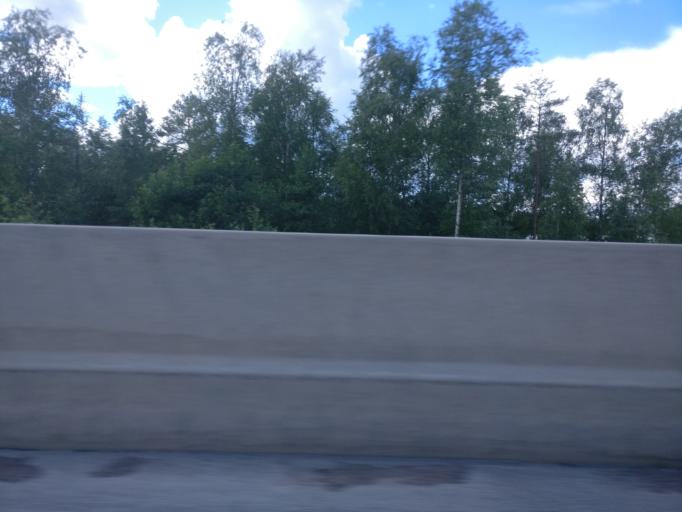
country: FI
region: Paijanne Tavastia
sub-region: Lahti
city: Heinola
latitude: 61.3721
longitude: 26.0508
